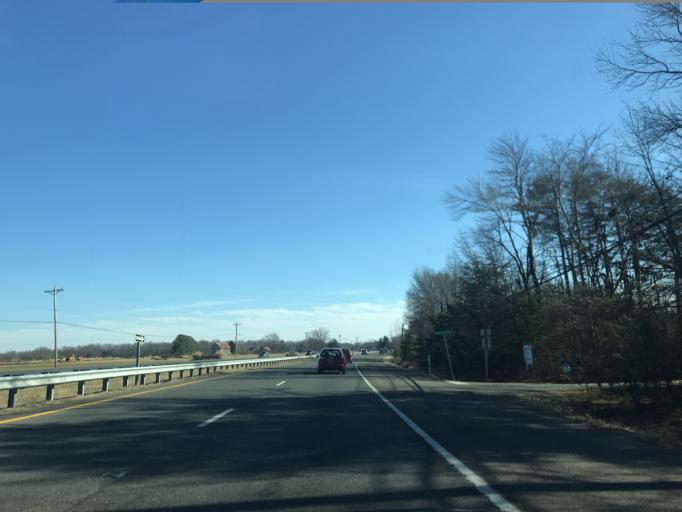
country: US
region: Maryland
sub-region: Charles County
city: Waldorf
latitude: 38.6454
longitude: -76.9353
